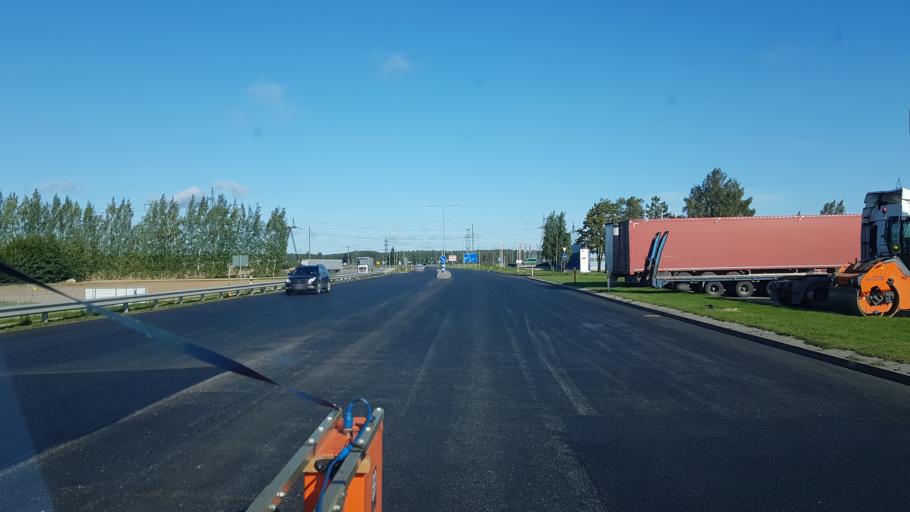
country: EE
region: Tartu
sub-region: Tartu linn
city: Tartu
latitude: 58.3763
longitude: 26.6821
